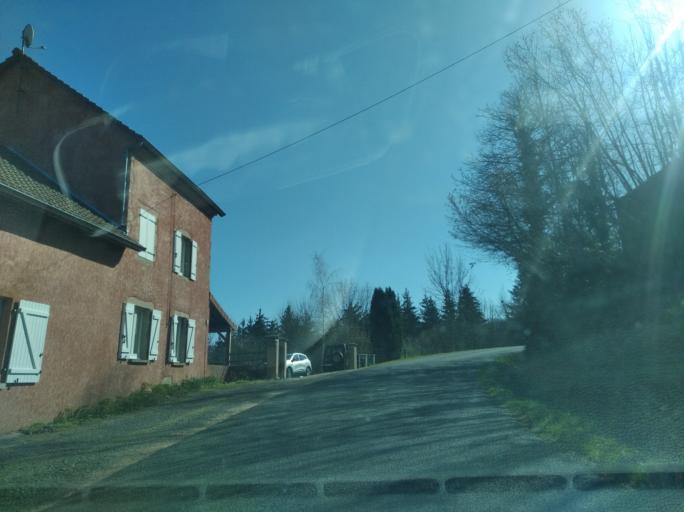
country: FR
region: Auvergne
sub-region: Departement de l'Allier
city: Le Mayet-de-Montagne
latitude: 46.0762
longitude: 3.6738
